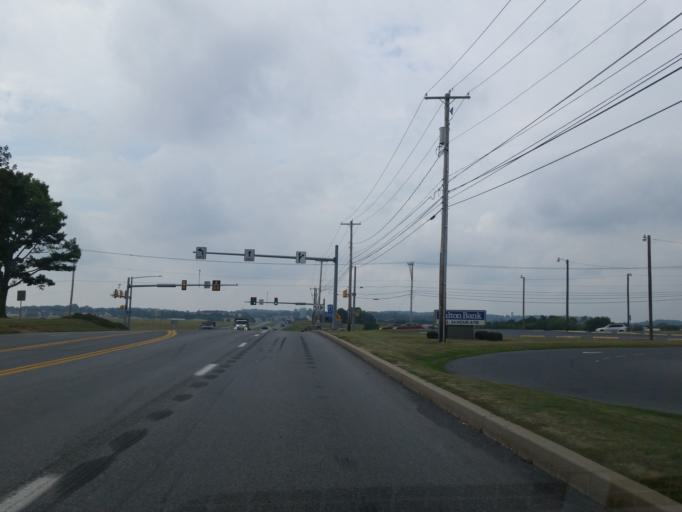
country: US
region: Pennsylvania
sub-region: Lancaster County
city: Lititz
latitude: 40.1276
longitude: -76.3051
